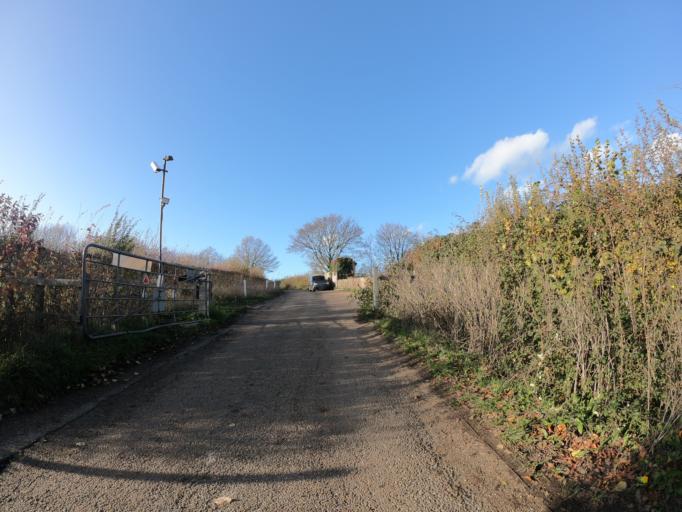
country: GB
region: England
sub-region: Kent
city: Eynsford
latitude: 51.3697
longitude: 0.1947
